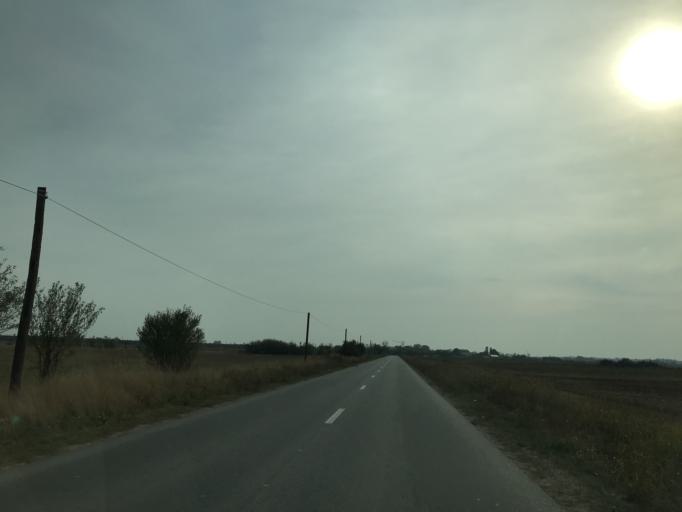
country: RO
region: Olt
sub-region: Comuna Slatioara
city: Slatioara
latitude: 44.3854
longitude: 24.3202
